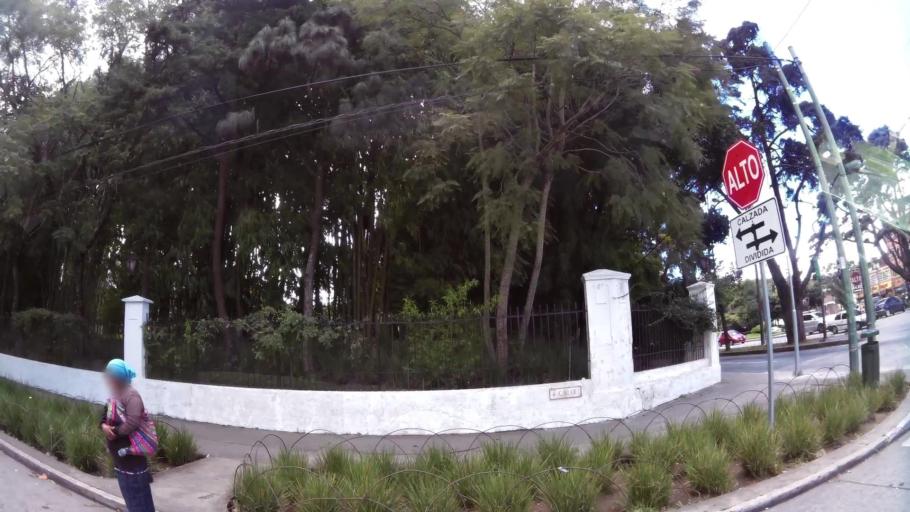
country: GT
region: Guatemala
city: Guatemala City
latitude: 14.6101
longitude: -90.5145
